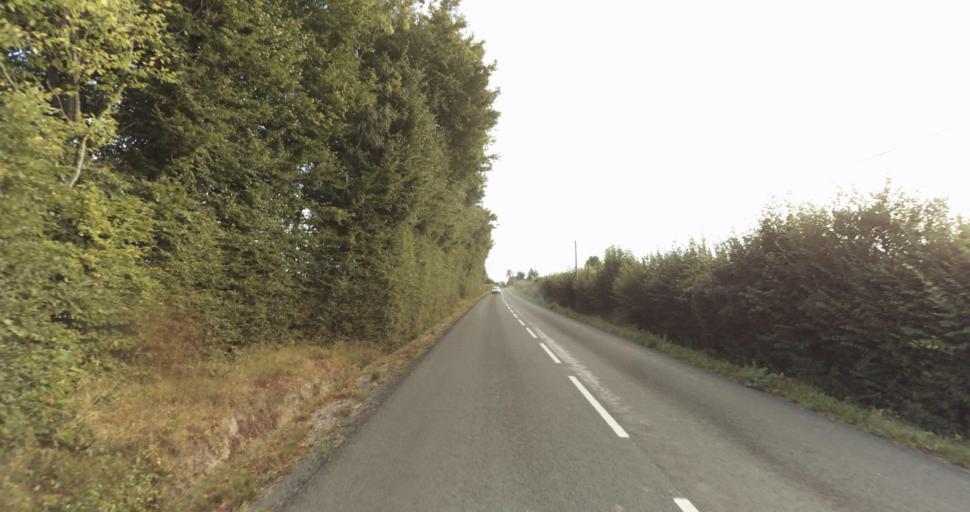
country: FR
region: Lower Normandy
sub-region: Departement de l'Orne
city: Vimoutiers
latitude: 48.9448
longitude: 0.2428
